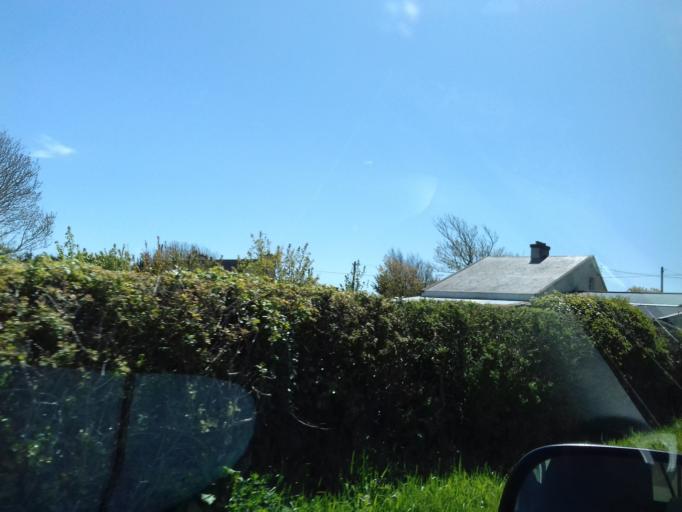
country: IE
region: Munster
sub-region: Waterford
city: Dunmore East
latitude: 52.1990
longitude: -6.8574
